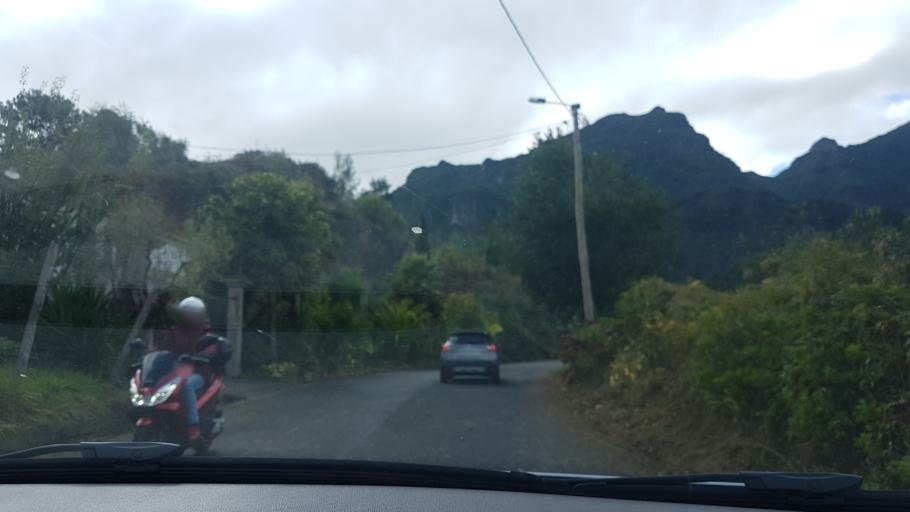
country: PT
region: Madeira
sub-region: Sao Vicente
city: Sao Vicente
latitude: 32.7750
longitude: -17.0274
